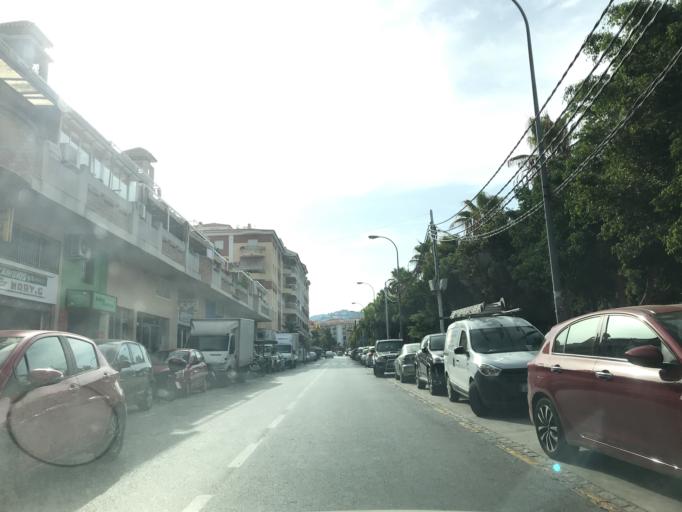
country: ES
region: Andalusia
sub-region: Provincia de Granada
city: Almunecar
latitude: 36.7358
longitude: -3.6850
